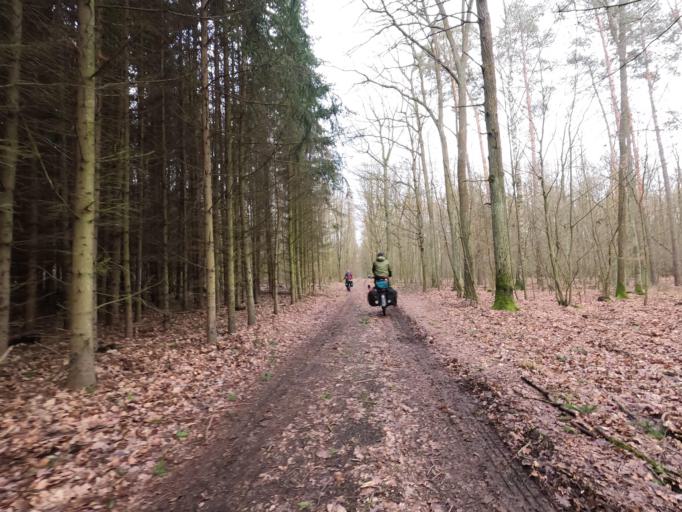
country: PL
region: Greater Poland Voivodeship
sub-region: Powiat pilski
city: Bialosliwie
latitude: 53.0948
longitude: 17.0887
